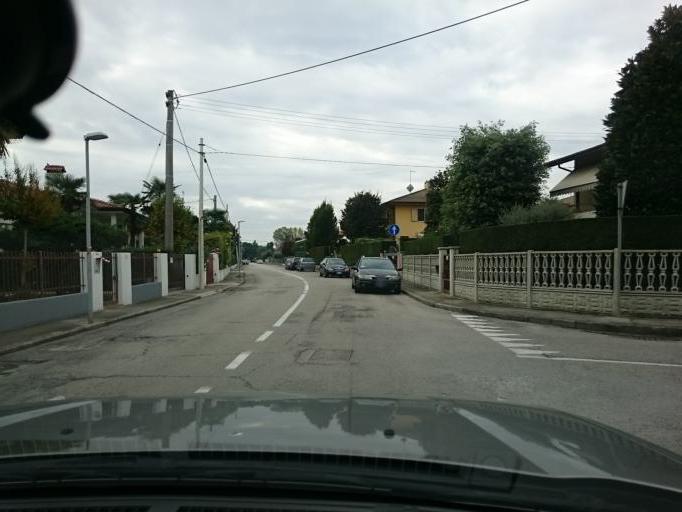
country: IT
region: Veneto
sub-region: Provincia di Padova
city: Ponte San Nicolo
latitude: 45.3719
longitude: 11.9274
